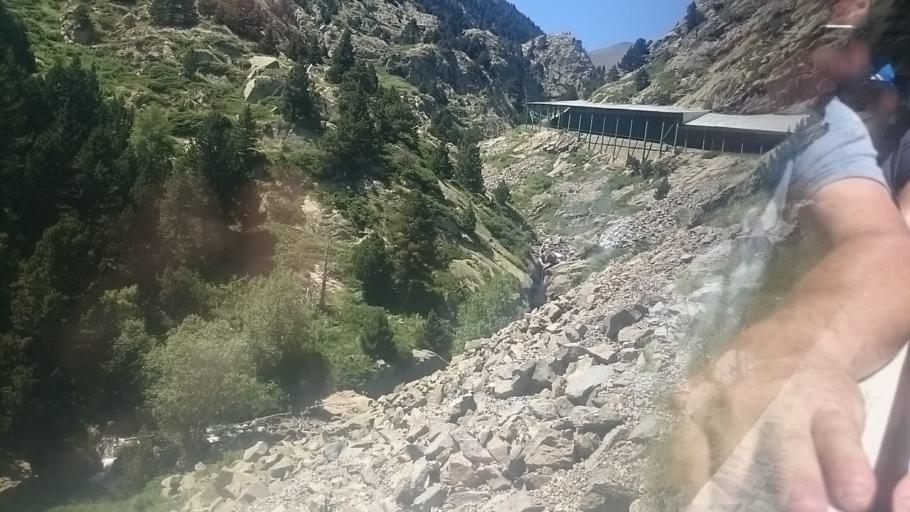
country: ES
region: Catalonia
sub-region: Provincia de Girona
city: Ribes de Freser
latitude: 42.3897
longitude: 2.1560
